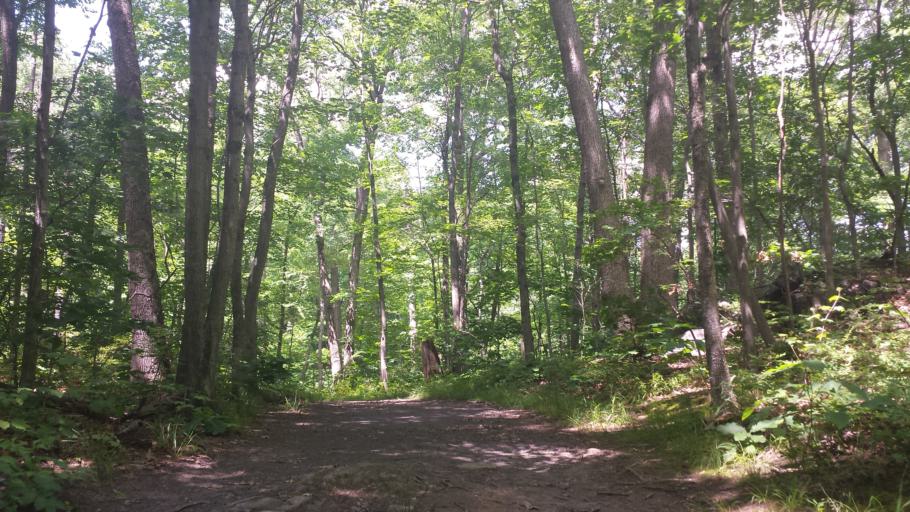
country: US
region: New York
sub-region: Westchester County
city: Mamaroneck
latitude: 40.9825
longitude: -73.7480
